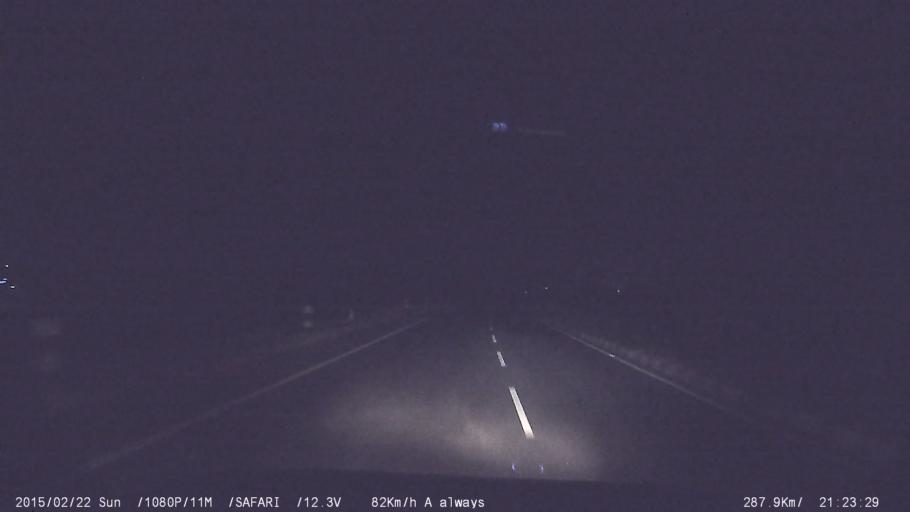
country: IN
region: Tamil Nadu
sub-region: Karur
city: Karur
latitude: 10.8807
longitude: 78.0097
